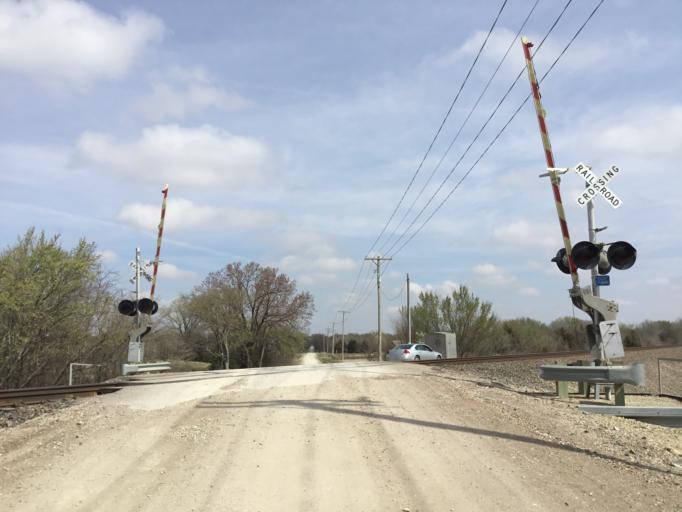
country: US
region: Kansas
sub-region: Butler County
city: Rose Hill
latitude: 37.5738
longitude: -97.1168
